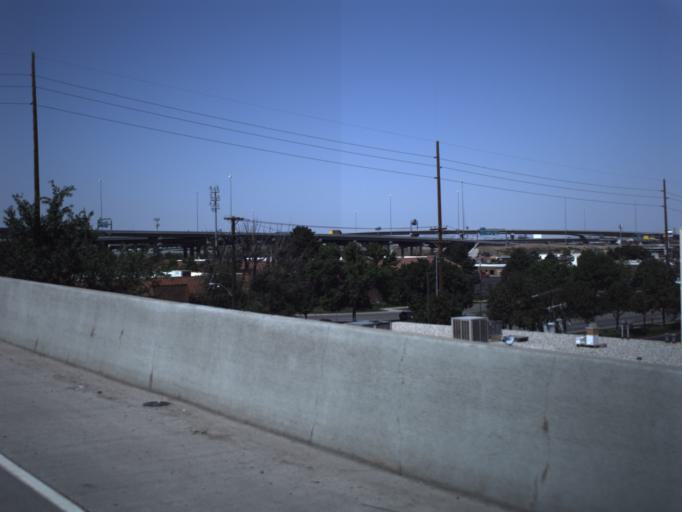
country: US
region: Utah
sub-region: Salt Lake County
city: South Salt Lake
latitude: 40.7186
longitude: -111.8987
